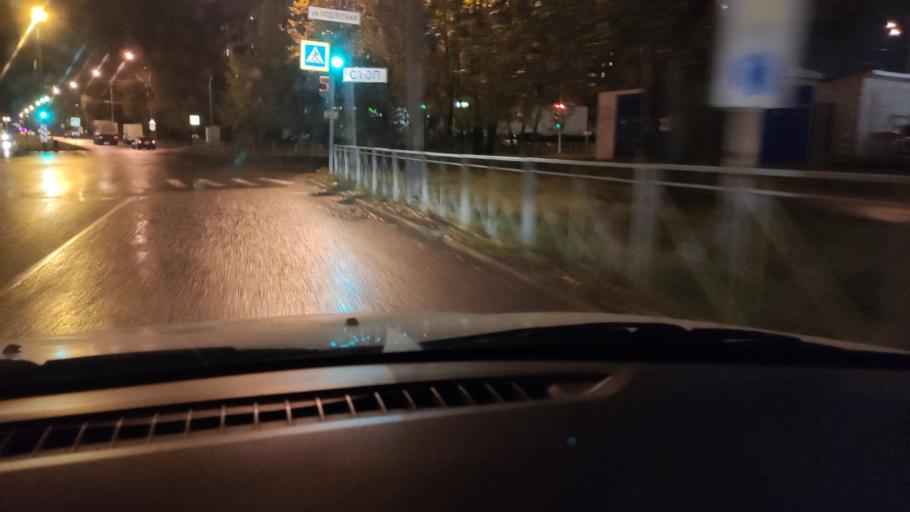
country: RU
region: Perm
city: Kondratovo
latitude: 57.9922
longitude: 56.1369
